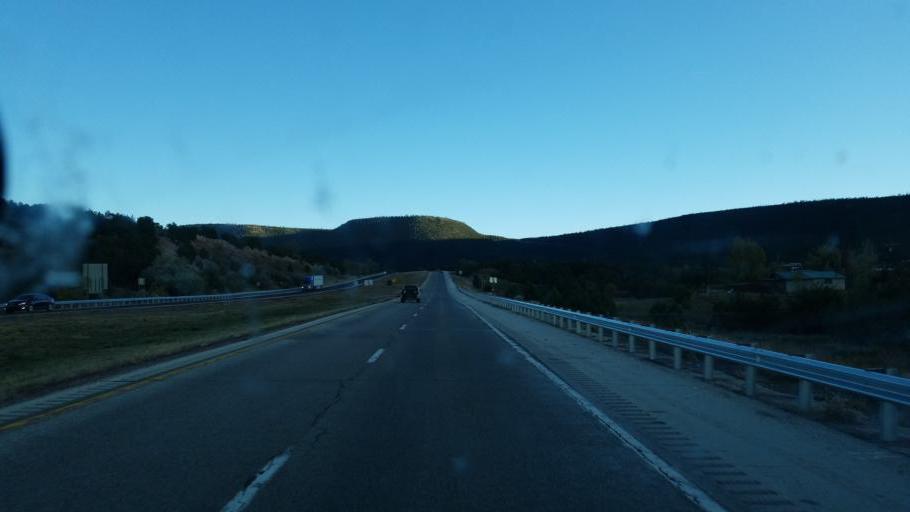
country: US
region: New Mexico
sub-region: San Miguel County
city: Pecos
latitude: 35.4892
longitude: -105.6719
